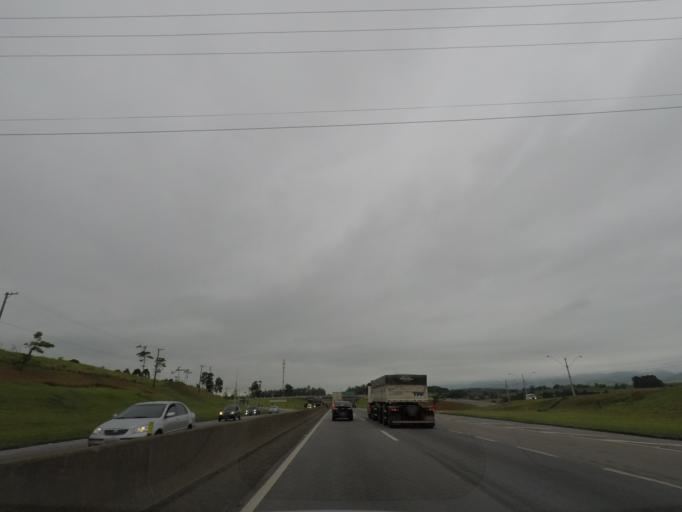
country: BR
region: Sao Paulo
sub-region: Pindamonhangaba
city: Pindamonhangaba
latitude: -22.9832
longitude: -45.4661
